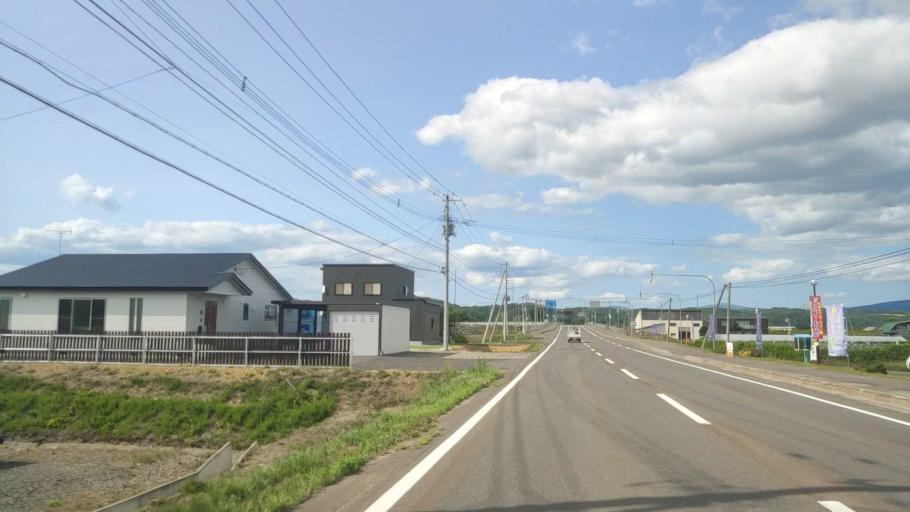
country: JP
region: Hokkaido
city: Nayoro
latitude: 44.3692
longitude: 142.4361
